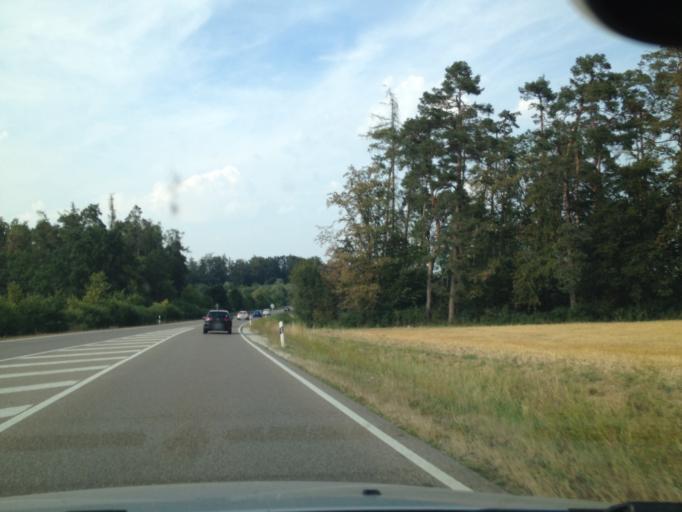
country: DE
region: Bavaria
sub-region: Swabia
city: Kaisheim
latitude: 48.7714
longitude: 10.7764
